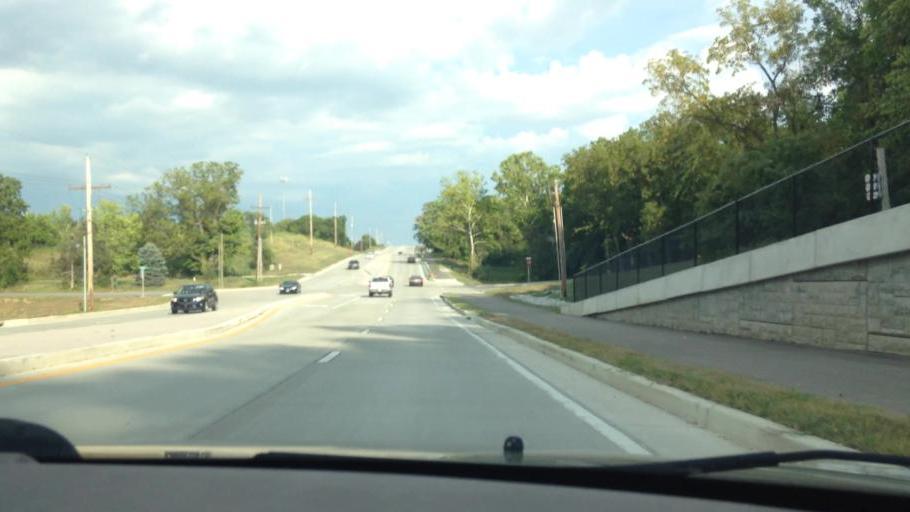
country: US
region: Missouri
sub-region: Platte County
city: Weatherby Lake
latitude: 39.2230
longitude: -94.7447
